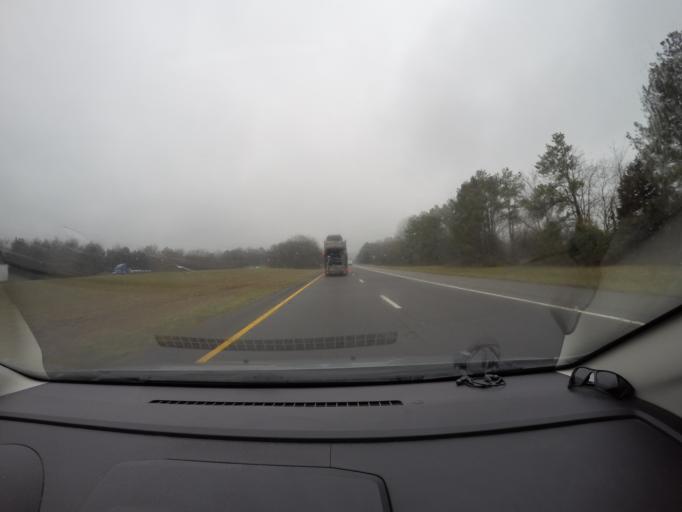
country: US
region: Tennessee
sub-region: Rutherford County
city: Plainview
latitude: 35.6164
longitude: -86.2410
